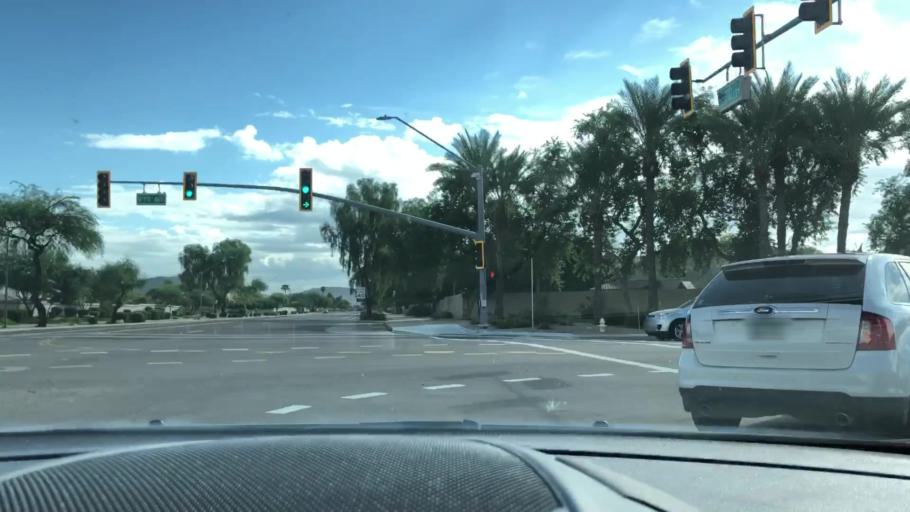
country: US
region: Arizona
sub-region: Maricopa County
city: Sun City
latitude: 33.6816
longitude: -112.2206
